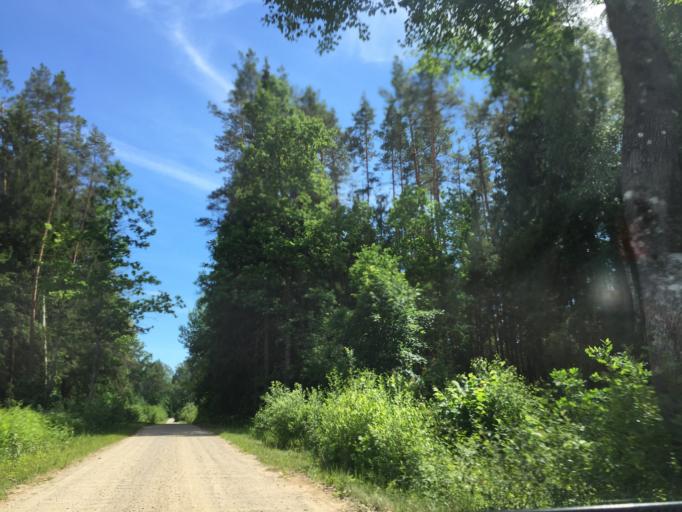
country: LV
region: Kuldigas Rajons
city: Kuldiga
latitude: 57.1210
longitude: 21.8699
